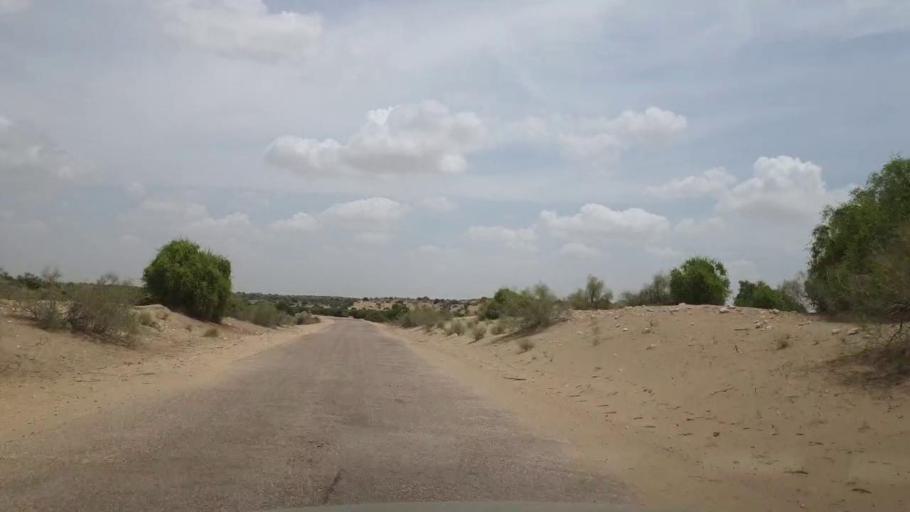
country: PK
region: Sindh
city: Kot Diji
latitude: 27.1848
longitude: 69.1714
